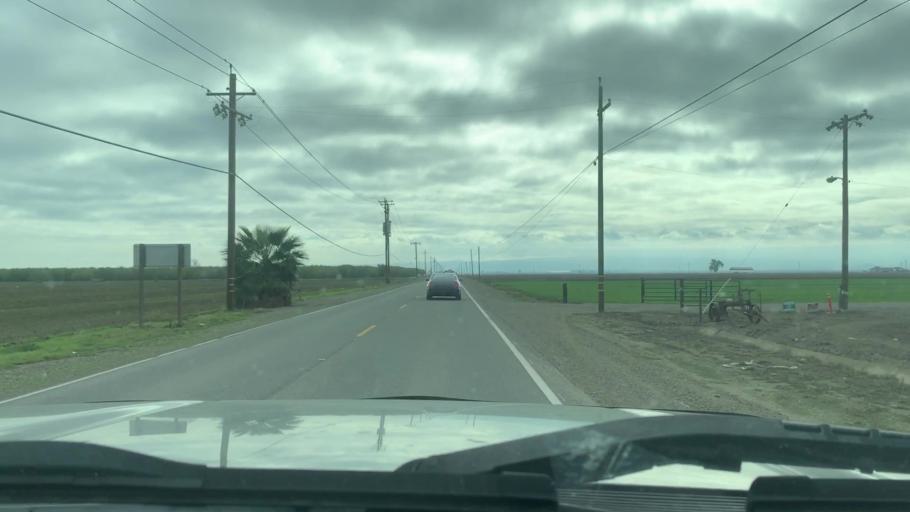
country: US
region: California
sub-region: Merced County
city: Los Banos
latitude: 37.0262
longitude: -120.8362
